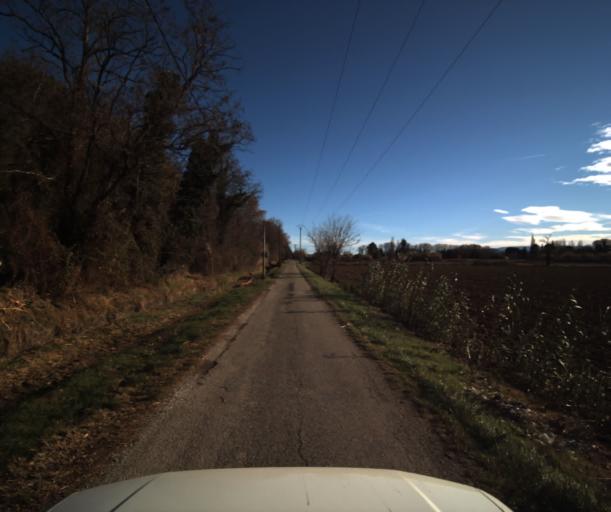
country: FR
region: Provence-Alpes-Cote d'Azur
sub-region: Departement du Vaucluse
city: Pertuis
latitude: 43.6948
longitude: 5.4794
